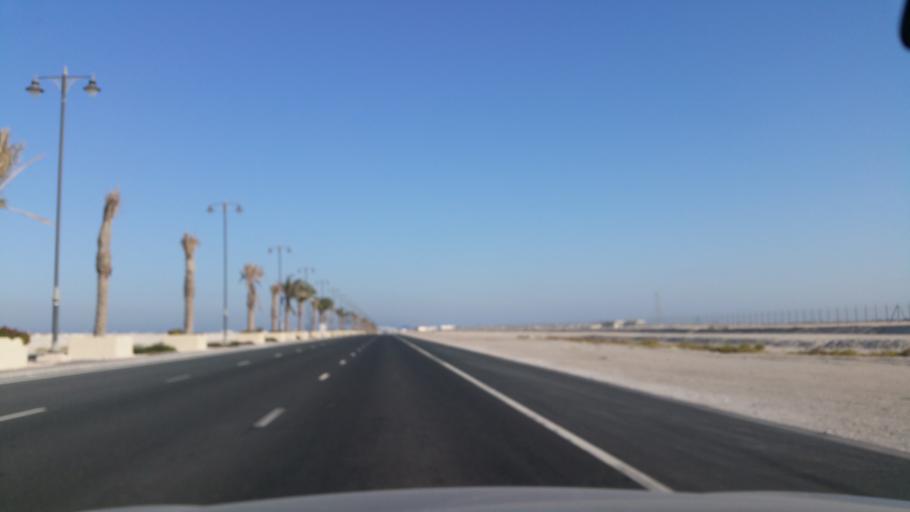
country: QA
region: Al Wakrah
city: Umm Sa'id
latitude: 25.0585
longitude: 51.5921
